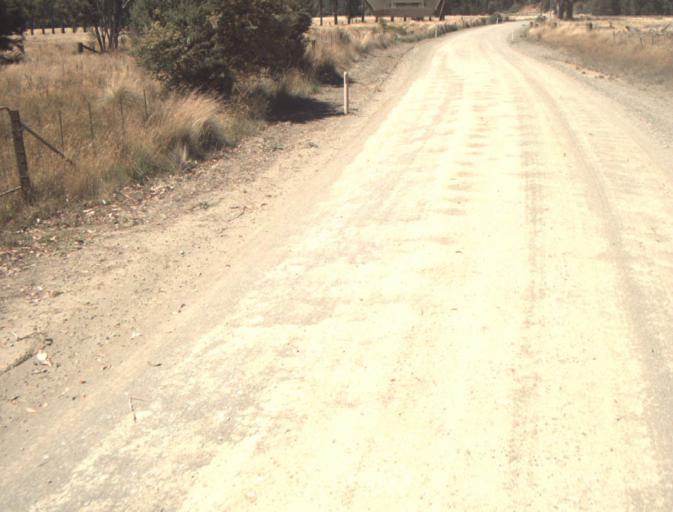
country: AU
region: Tasmania
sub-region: Dorset
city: Scottsdale
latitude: -41.2938
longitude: 147.3948
